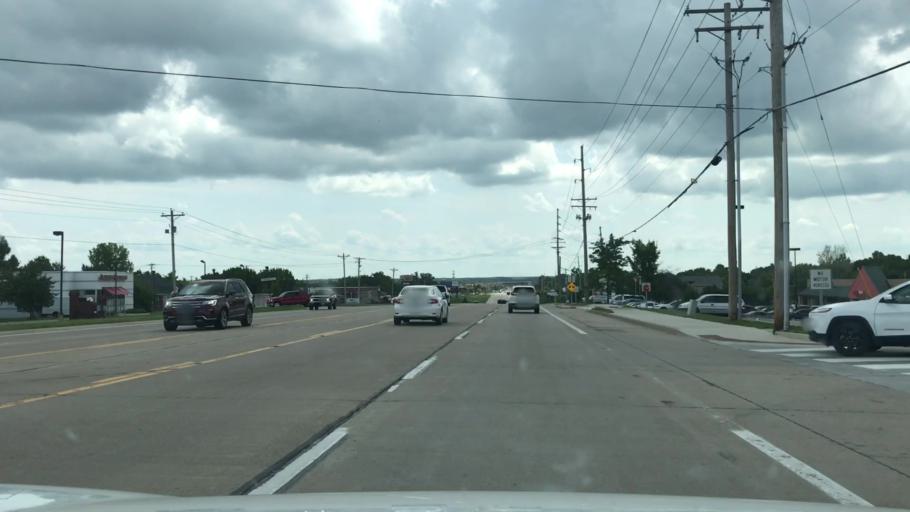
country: US
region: Missouri
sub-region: Saint Charles County
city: Dardenne Prairie
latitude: 38.7700
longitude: -90.7002
